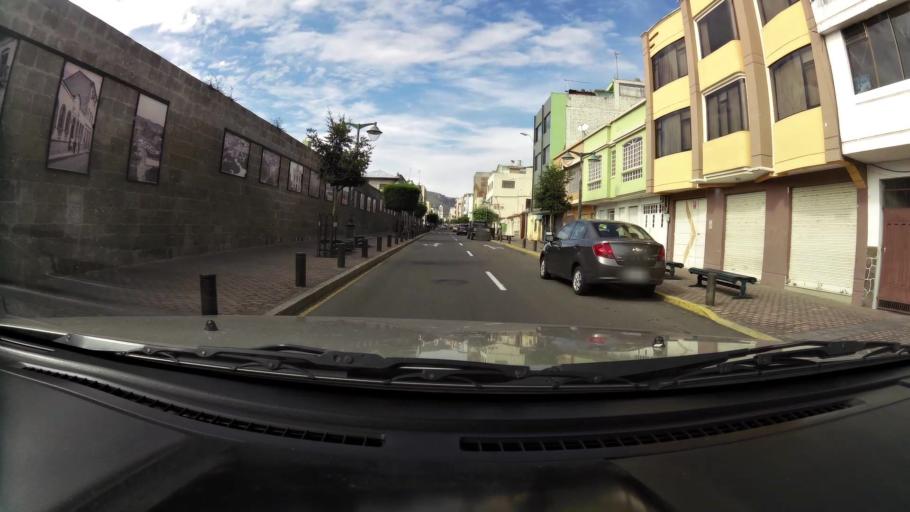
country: EC
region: Tungurahua
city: Ambato
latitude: -1.2364
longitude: -78.6240
